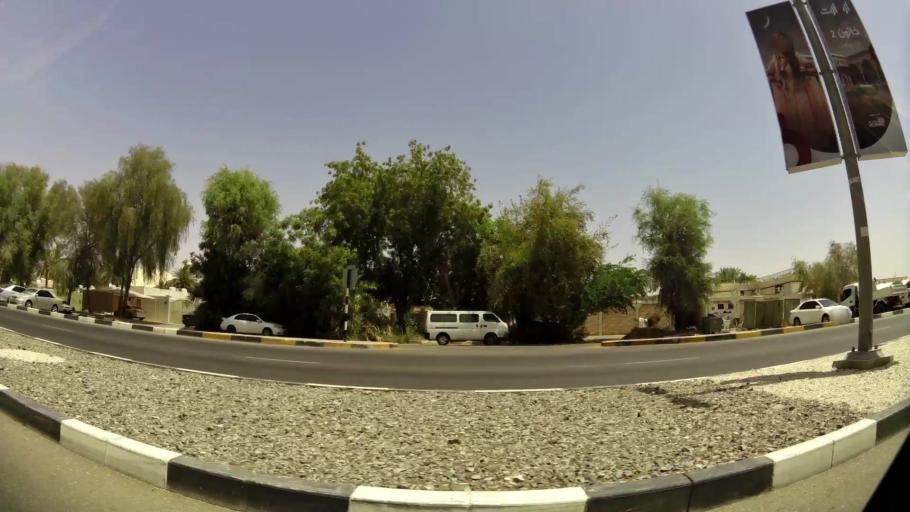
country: OM
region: Al Buraimi
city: Al Buraymi
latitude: 24.2649
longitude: 55.7580
